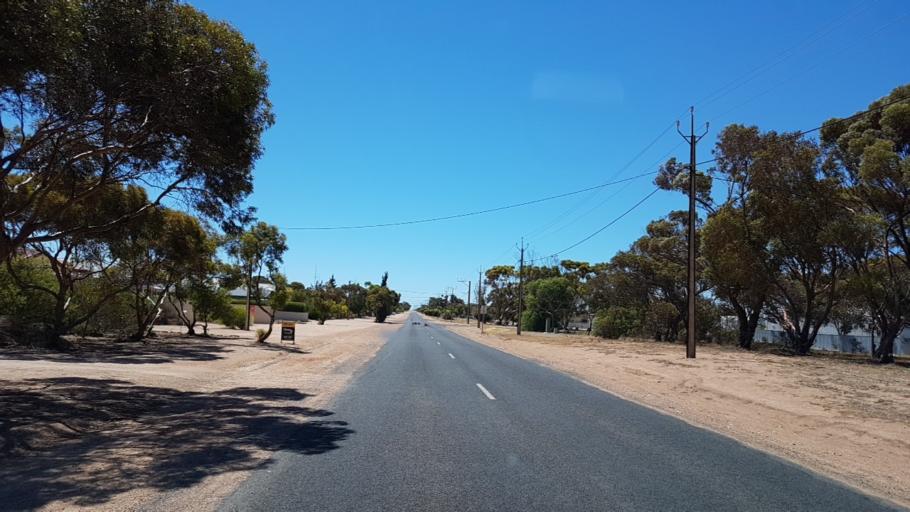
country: AU
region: South Australia
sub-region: Copper Coast
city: Wallaroo
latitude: -34.0606
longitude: 137.5931
